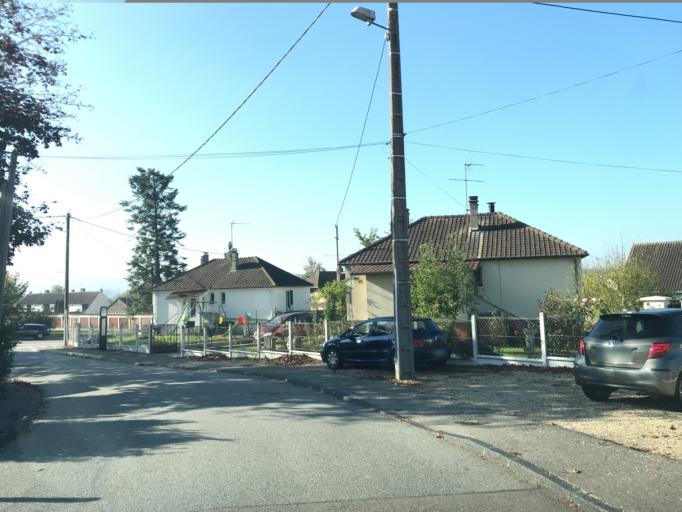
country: FR
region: Haute-Normandie
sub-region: Departement de l'Eure
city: Louviers
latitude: 49.2077
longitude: 1.1879
